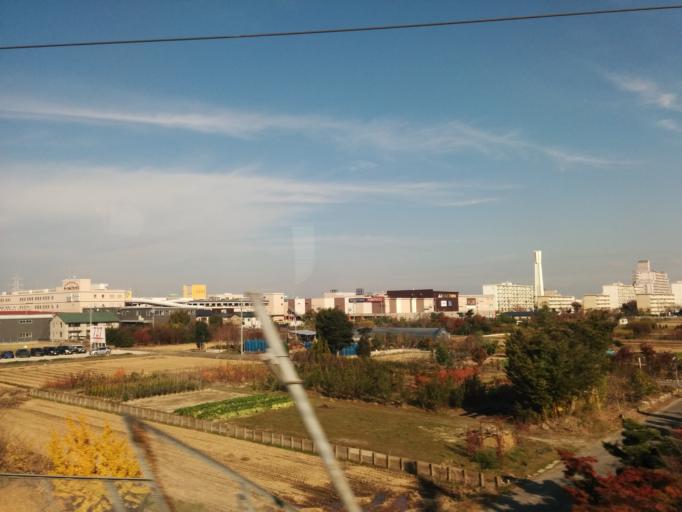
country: JP
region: Aichi
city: Inazawa
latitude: 35.2490
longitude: 136.7694
